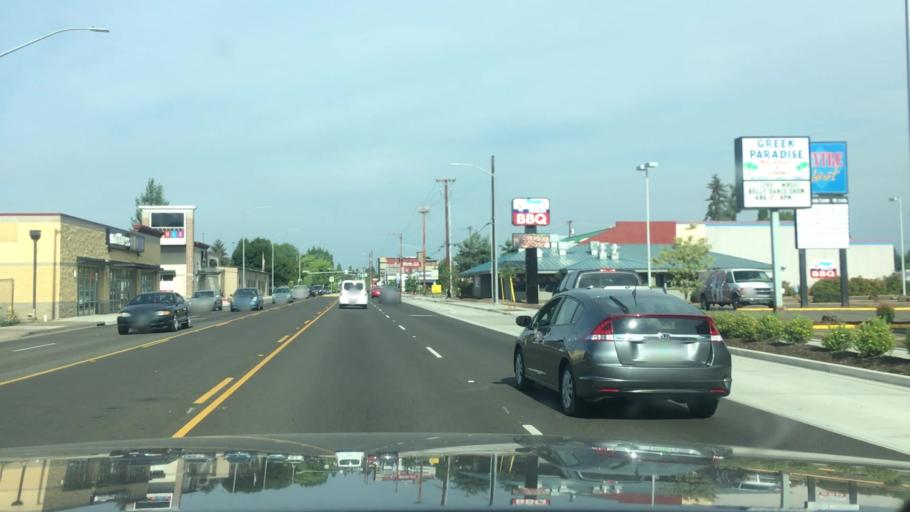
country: US
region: Oregon
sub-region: Lane County
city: Eugene
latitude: 44.0478
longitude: -123.1266
